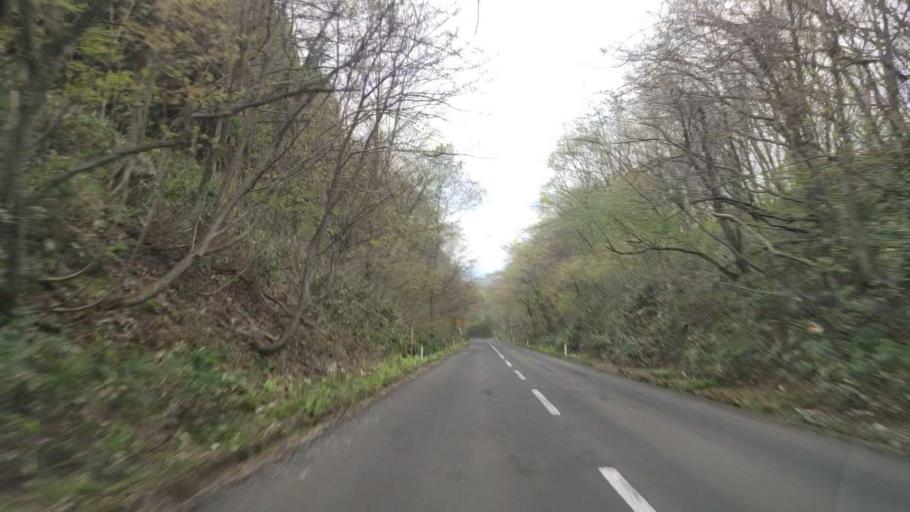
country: JP
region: Akita
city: Hanawa
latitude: 40.3837
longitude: 140.7921
